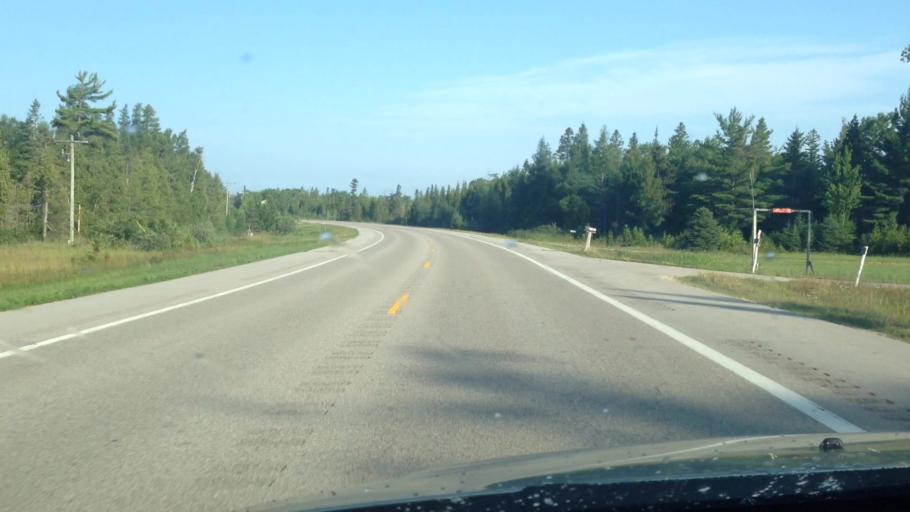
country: US
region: Michigan
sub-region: Mackinac County
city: Saint Ignace
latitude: 45.8994
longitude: -84.8374
